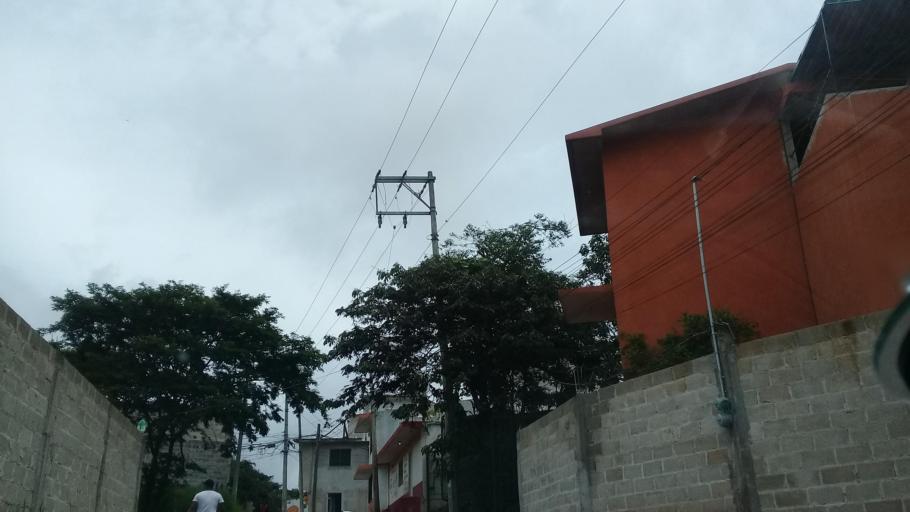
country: MX
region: Veracruz
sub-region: Emiliano Zapata
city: Las Trancas
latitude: 19.4993
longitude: -96.8690
